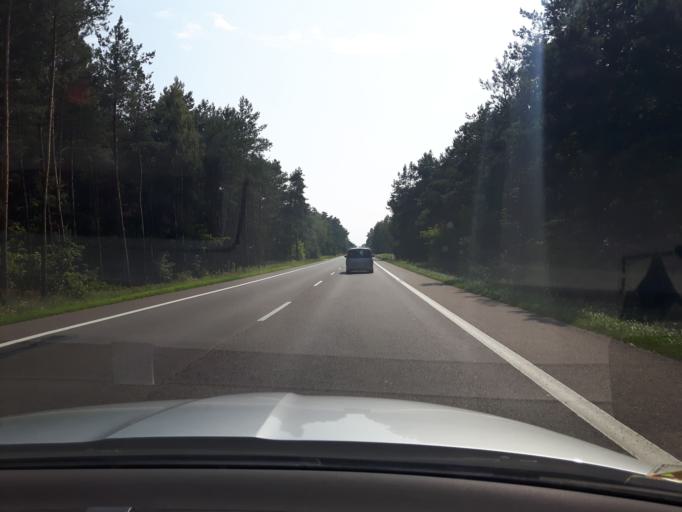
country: PL
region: Masovian Voivodeship
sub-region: Powiat ciechanowski
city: Glinojeck
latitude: 52.8533
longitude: 20.2836
